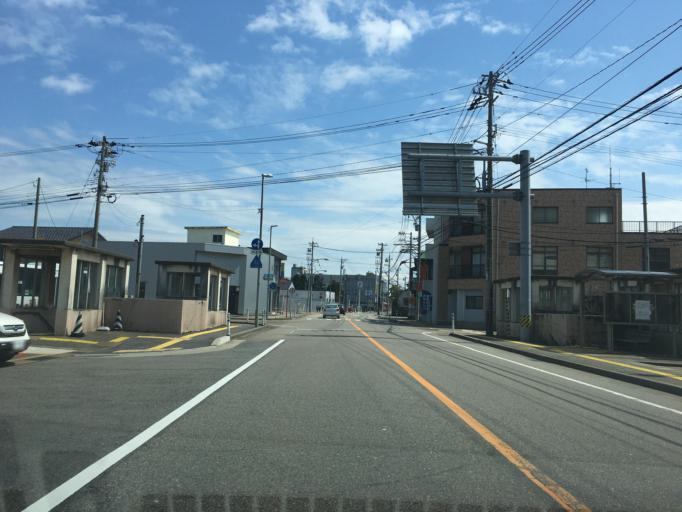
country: JP
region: Toyama
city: Nishishinminato
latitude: 36.7822
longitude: 137.0793
